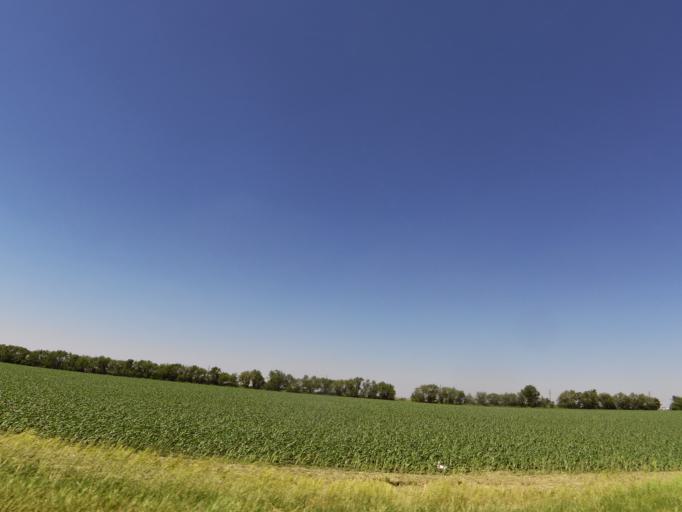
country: US
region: Illinois
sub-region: McLean County
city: Chenoa
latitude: 40.7412
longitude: -88.7475
